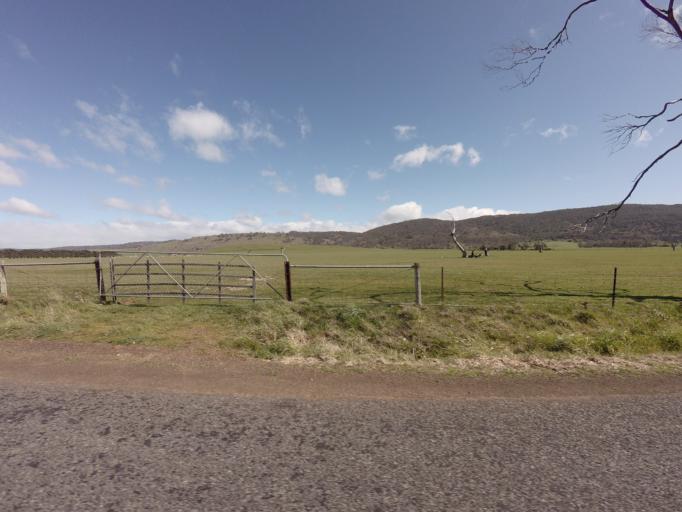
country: AU
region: Tasmania
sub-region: Northern Midlands
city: Evandale
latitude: -41.9903
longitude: 147.4523
